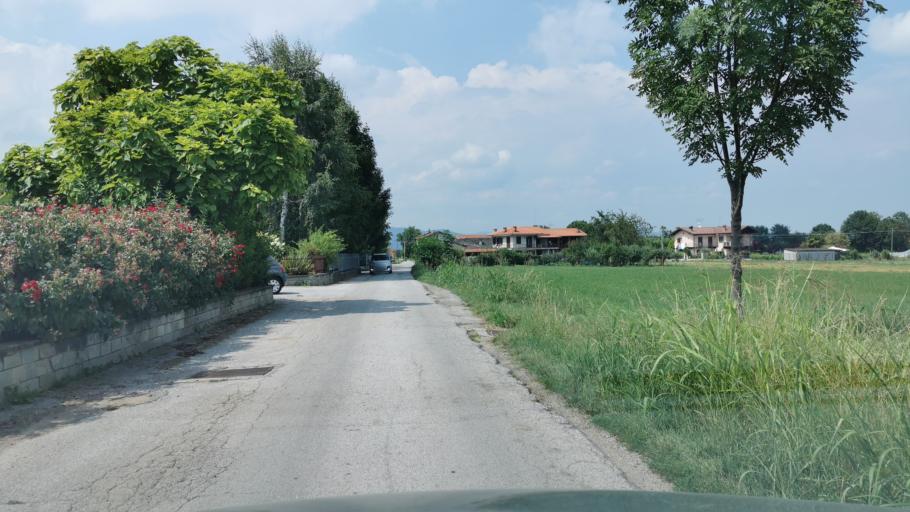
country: IT
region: Piedmont
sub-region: Provincia di Cuneo
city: Caraglio
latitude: 44.4247
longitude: 7.4529
